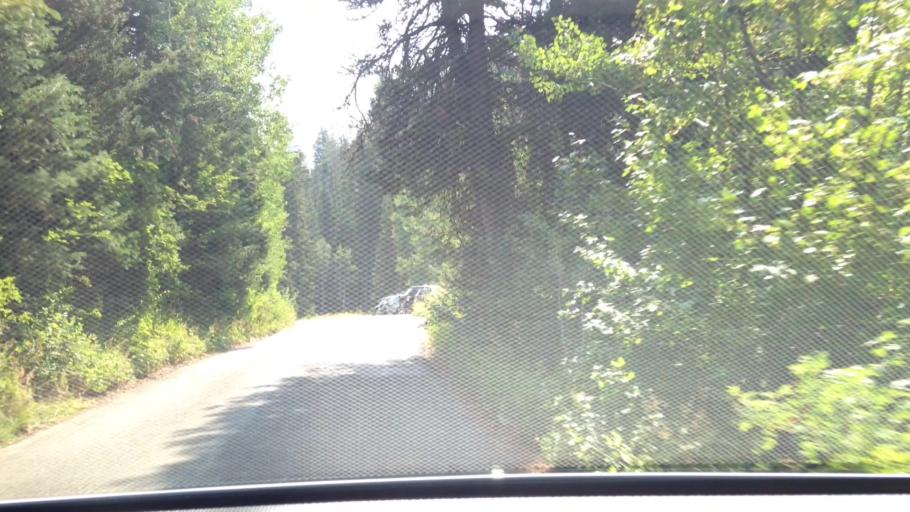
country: US
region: Utah
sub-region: Summit County
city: Summit Park
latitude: 40.6891
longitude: -111.6587
